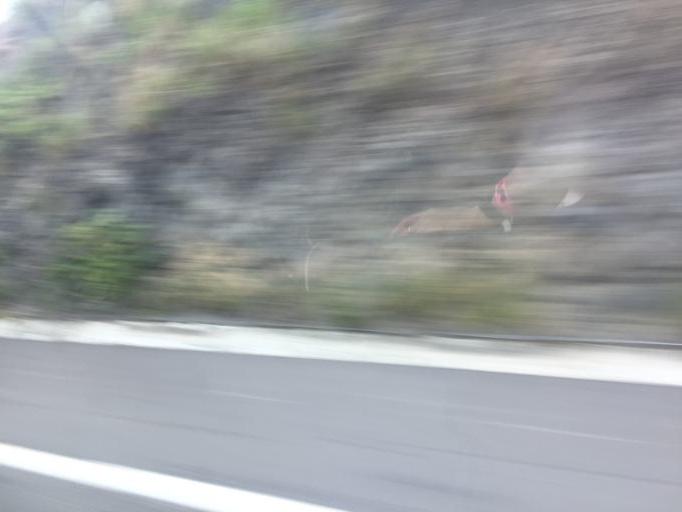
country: MX
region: Jalisco
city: Ocotlan
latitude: 20.4106
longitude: -102.7434
